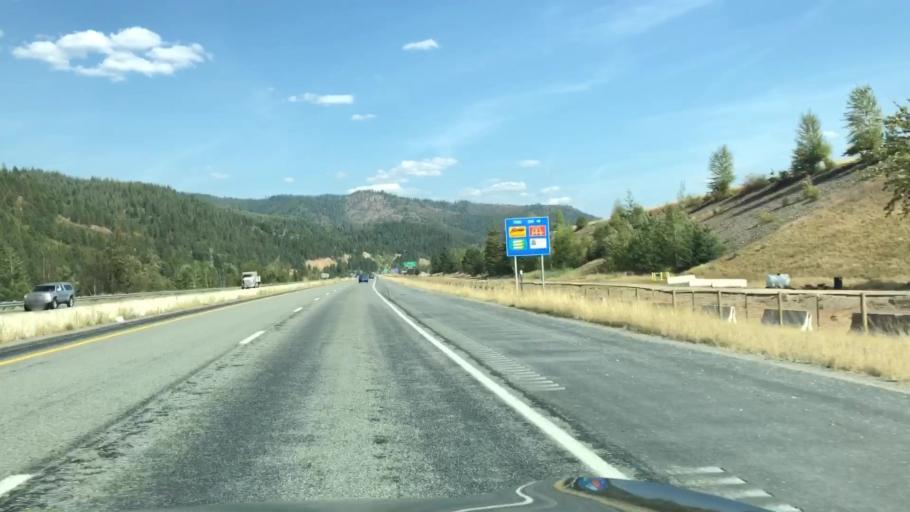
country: US
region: Idaho
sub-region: Shoshone County
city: Kellogg
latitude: 47.5480
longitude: -116.1582
